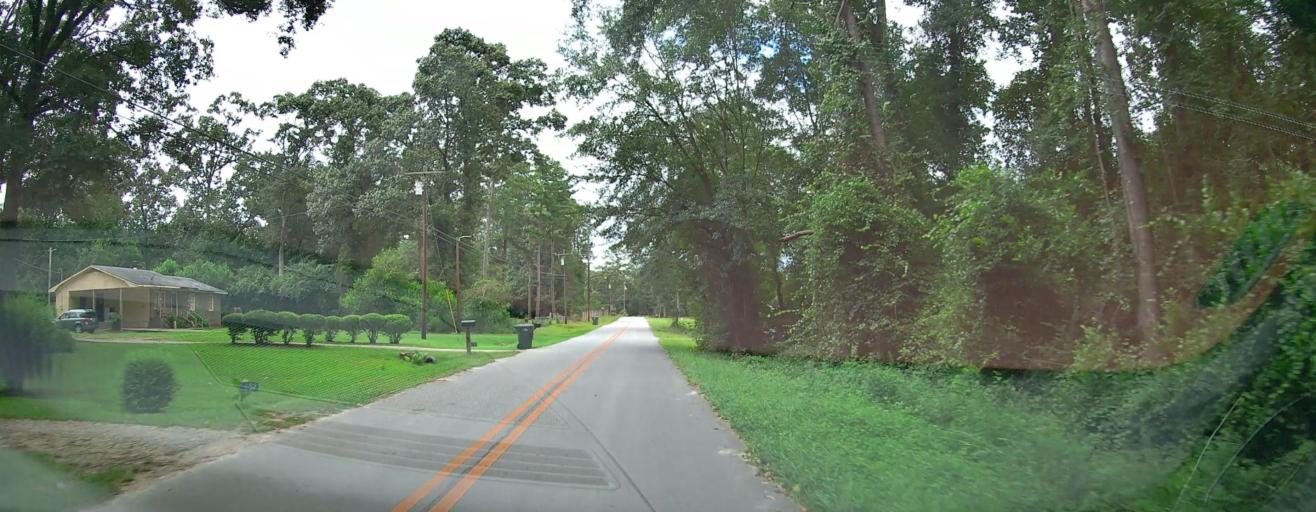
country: US
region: Georgia
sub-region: Twiggs County
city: Jeffersonville
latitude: 32.6750
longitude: -83.3234
